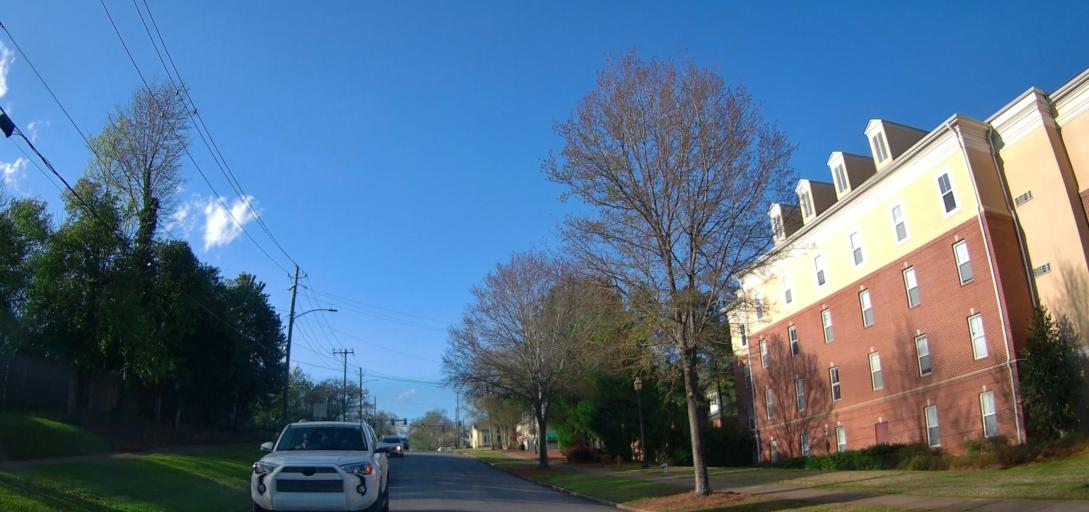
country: US
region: Georgia
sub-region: Baldwin County
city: Milledgeville
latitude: 33.0787
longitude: -83.2338
